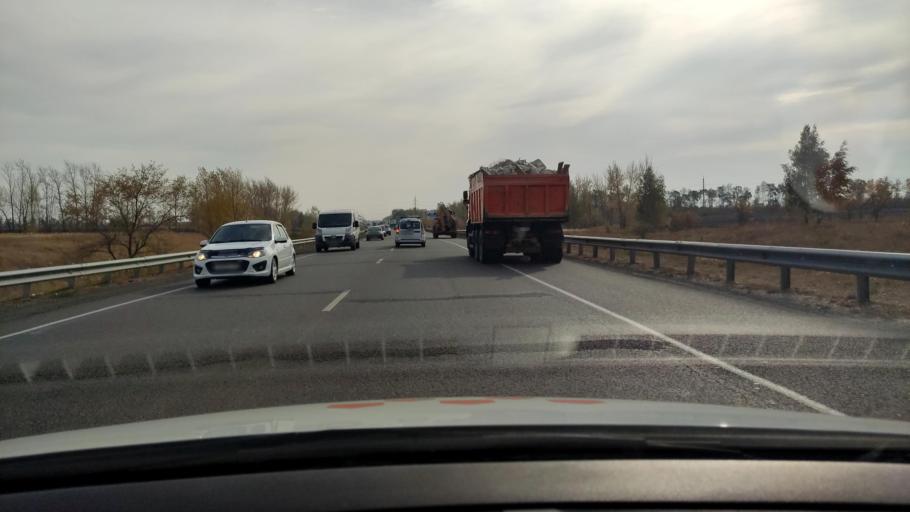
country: RU
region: Voronezj
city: Novaya Usman'
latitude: 51.6967
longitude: 39.4351
